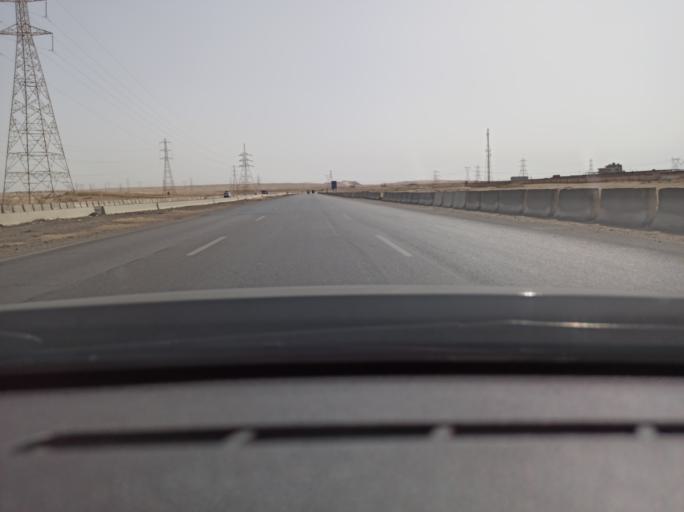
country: EG
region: Muhafazat al Qahirah
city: Halwan
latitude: 29.7668
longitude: 31.3901
